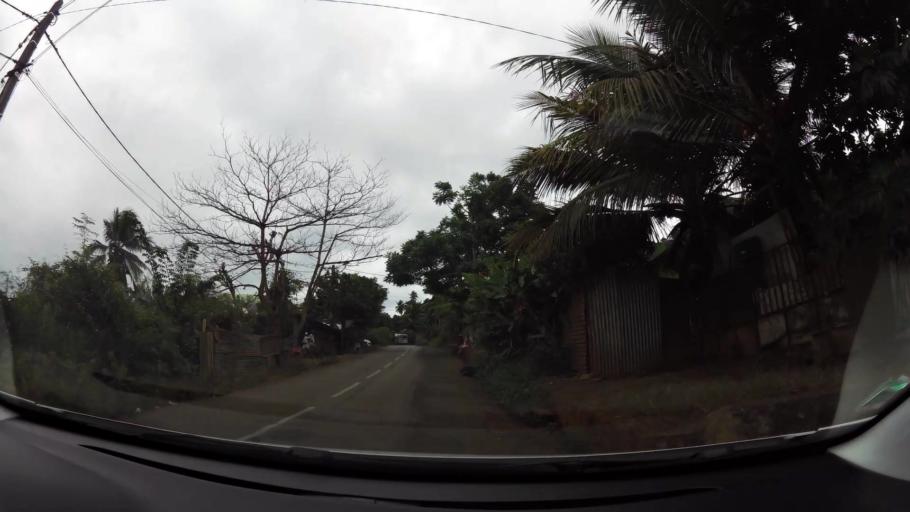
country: YT
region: Chiconi
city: Chiconi
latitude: -12.8376
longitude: 45.1192
